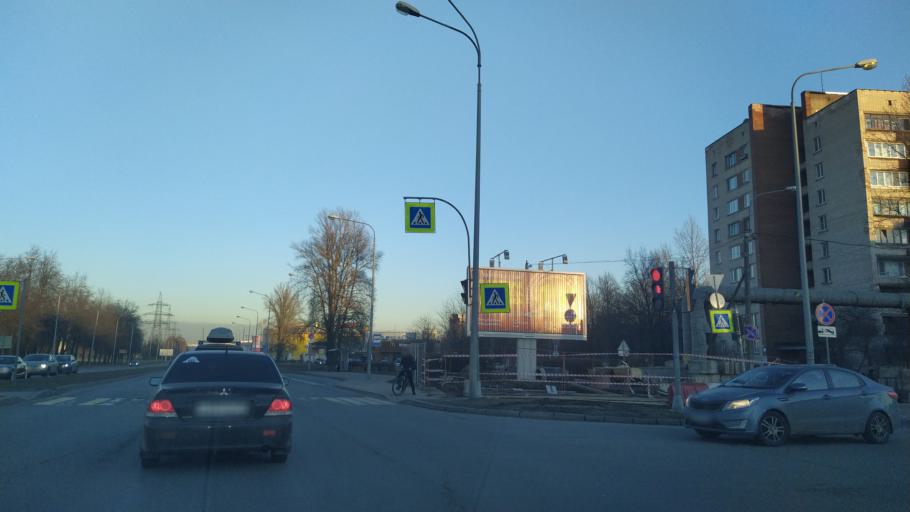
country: RU
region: Leningrad
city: Kalininskiy
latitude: 59.9765
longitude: 30.4023
